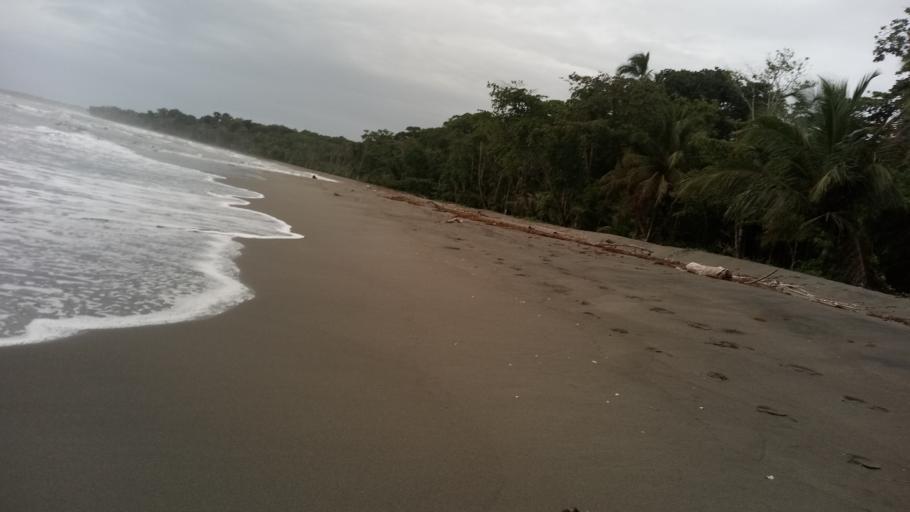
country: CR
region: Limon
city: Sixaola
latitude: 9.6176
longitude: -82.6206
